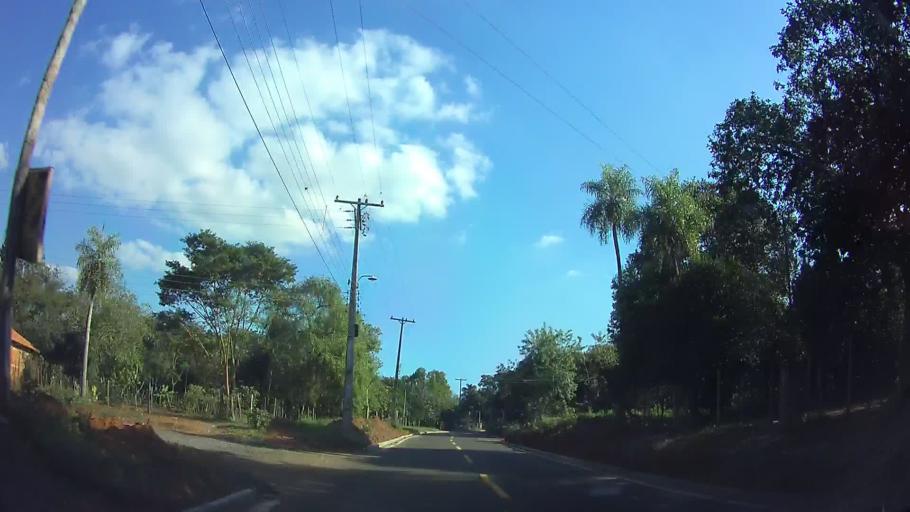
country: PY
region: Central
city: Aregua
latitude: -25.2740
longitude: -57.4402
